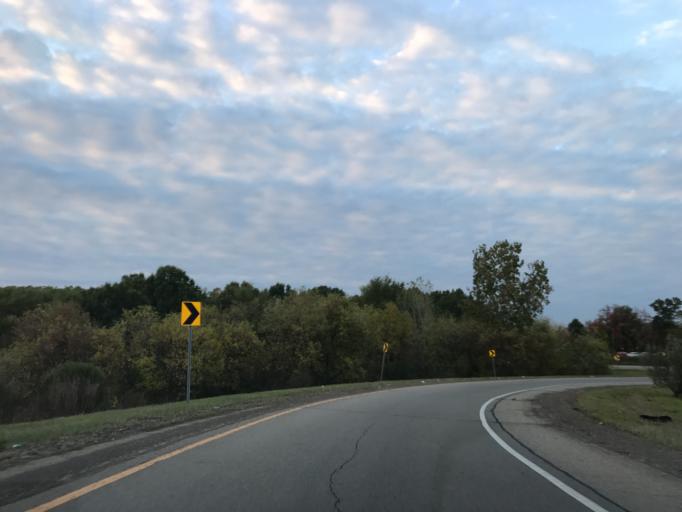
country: US
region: Michigan
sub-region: Oakland County
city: South Lyon
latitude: 42.5197
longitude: -83.6178
